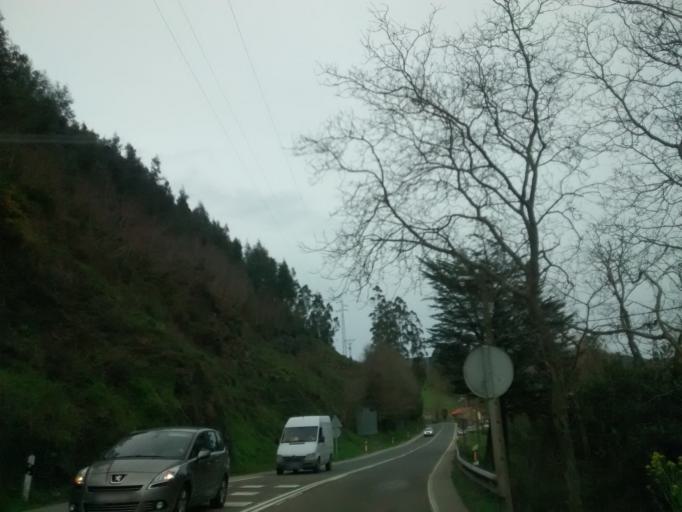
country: ES
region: Cantabria
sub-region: Provincia de Cantabria
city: Puente Viesgo
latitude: 43.3020
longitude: -3.9672
